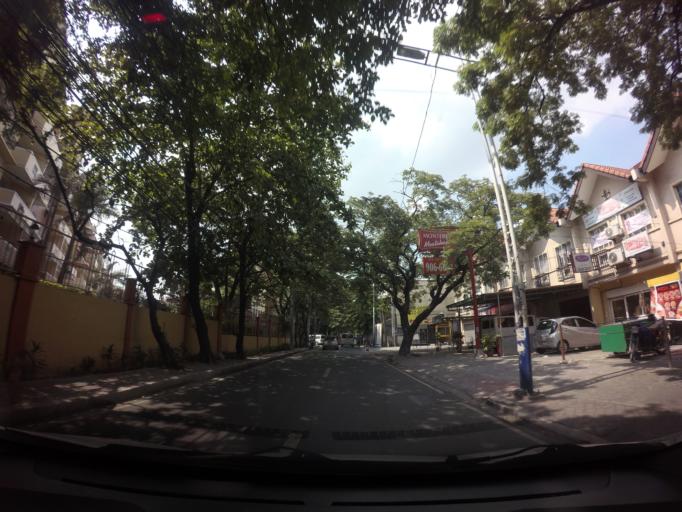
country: PH
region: Calabarzon
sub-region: Province of Rizal
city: Pateros
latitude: 14.5314
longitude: 121.0719
